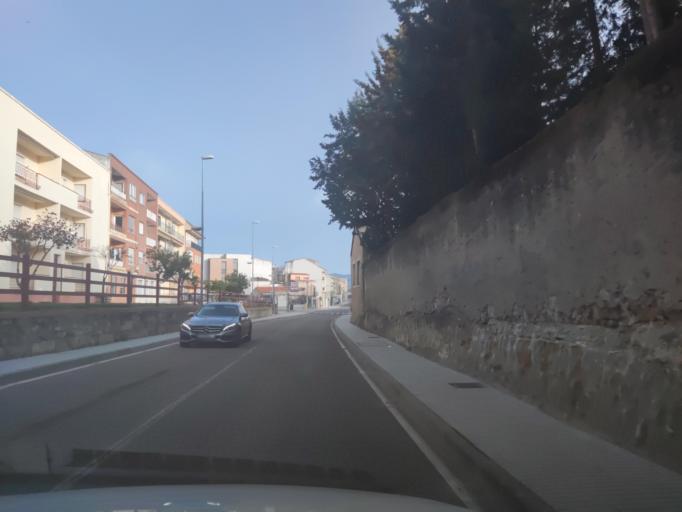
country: ES
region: Castille and Leon
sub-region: Provincia de Salamanca
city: Ciudad Rodrigo
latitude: 40.5973
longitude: -6.5270
